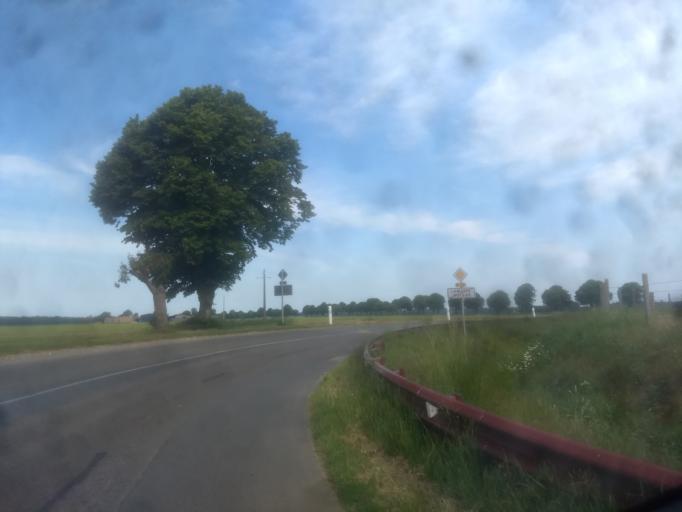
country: FR
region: Picardie
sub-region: Departement de la Somme
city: Nouvion
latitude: 50.1891
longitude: 1.8235
